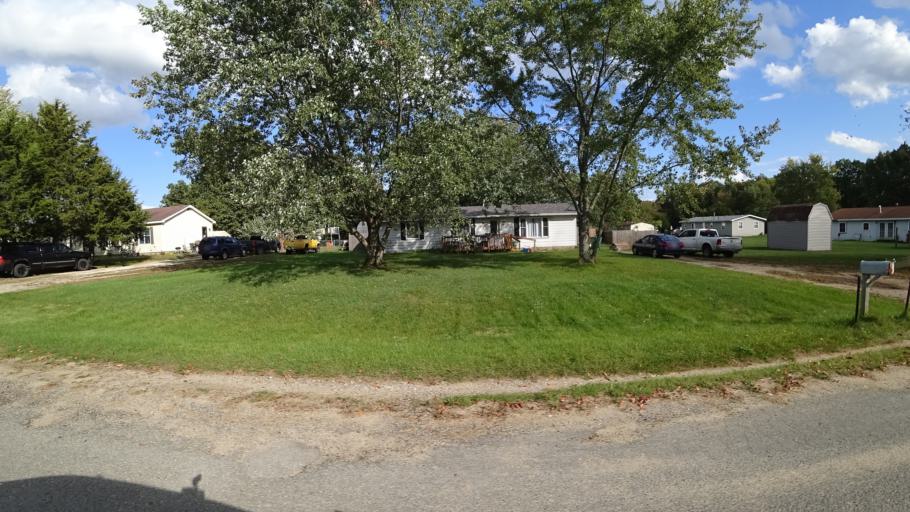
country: US
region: Michigan
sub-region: Saint Joseph County
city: Three Rivers
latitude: 41.9537
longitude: -85.5853
